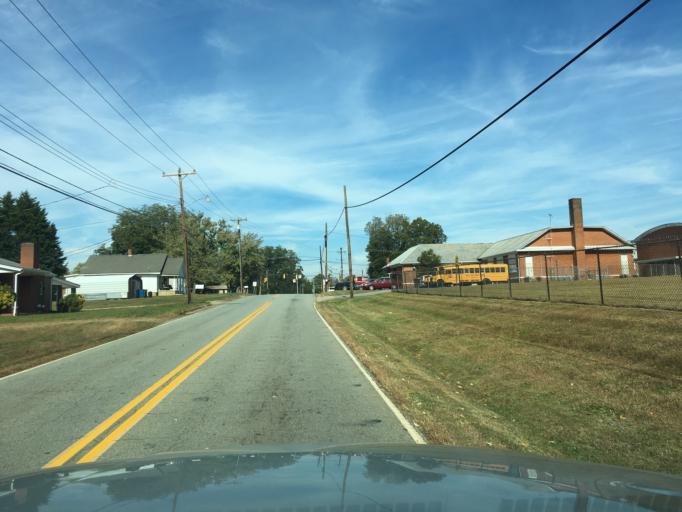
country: US
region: North Carolina
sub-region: Catawba County
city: Hickory
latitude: 35.7301
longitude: -81.2990
